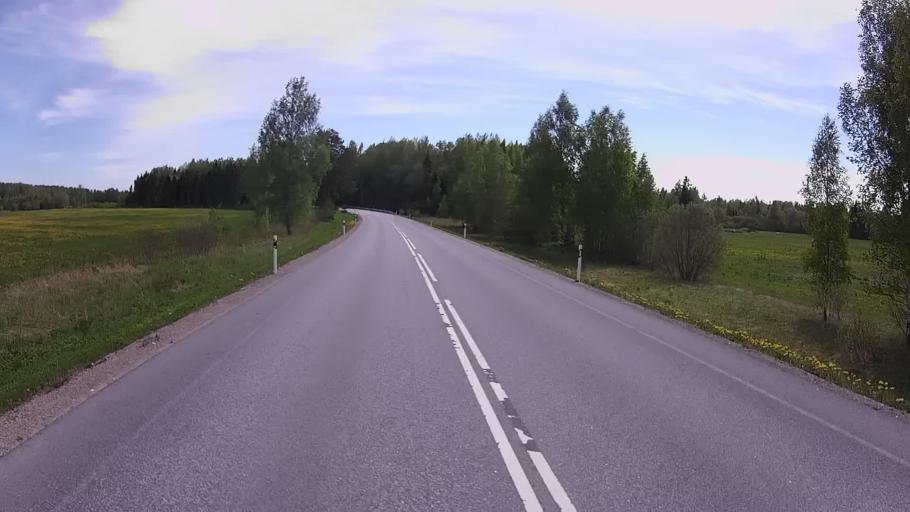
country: EE
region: Valgamaa
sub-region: Valga linn
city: Valga
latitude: 57.7361
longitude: 26.1458
